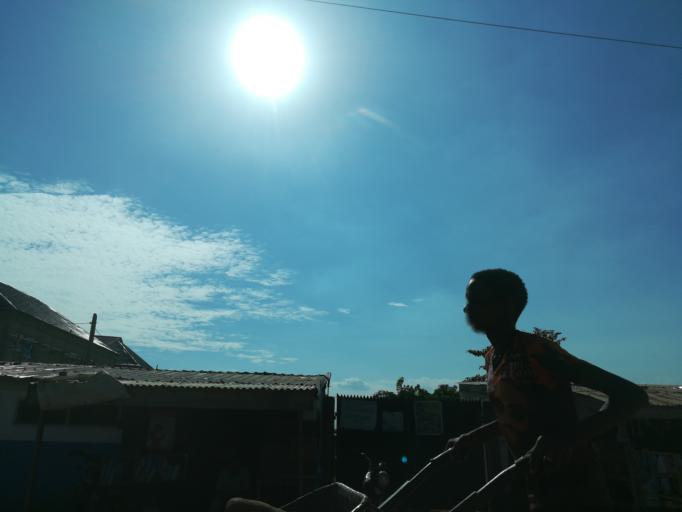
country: NG
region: Lagos
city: Ikorodu
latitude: 6.5846
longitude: 3.5221
